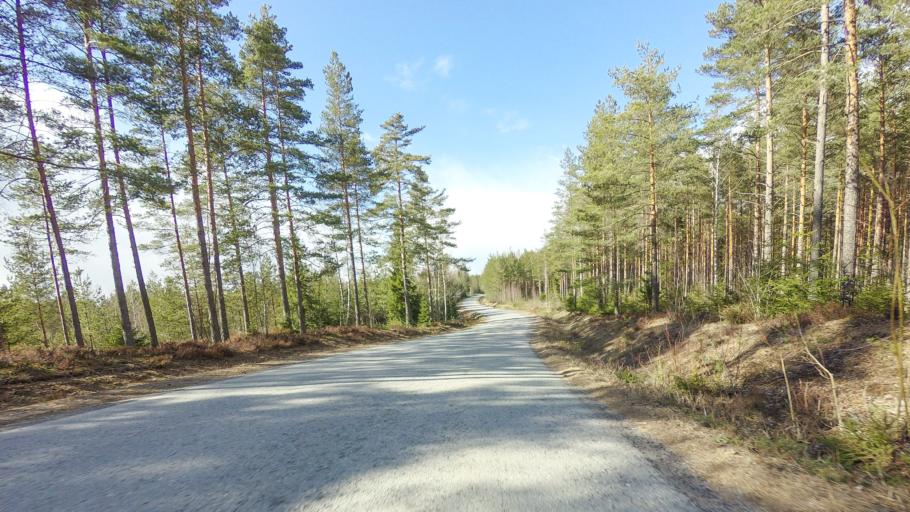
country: FI
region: Uusimaa
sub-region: Helsinki
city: Sammatti
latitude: 60.2767
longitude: 23.7781
